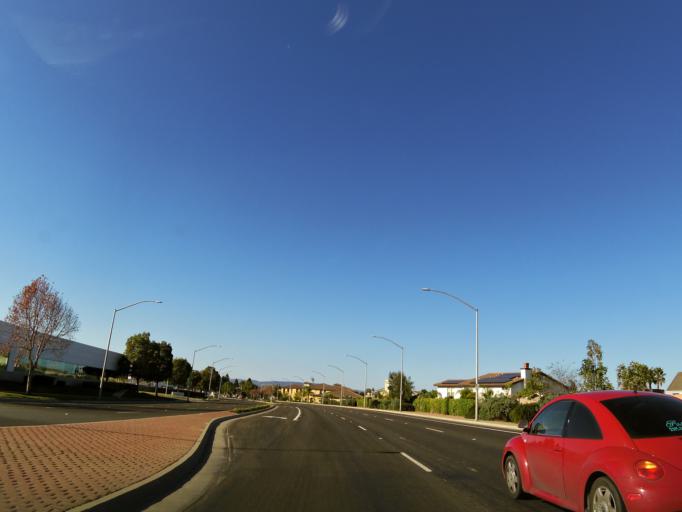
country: US
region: California
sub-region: Santa Barbara County
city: Santa Maria
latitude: 34.9237
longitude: -120.4276
